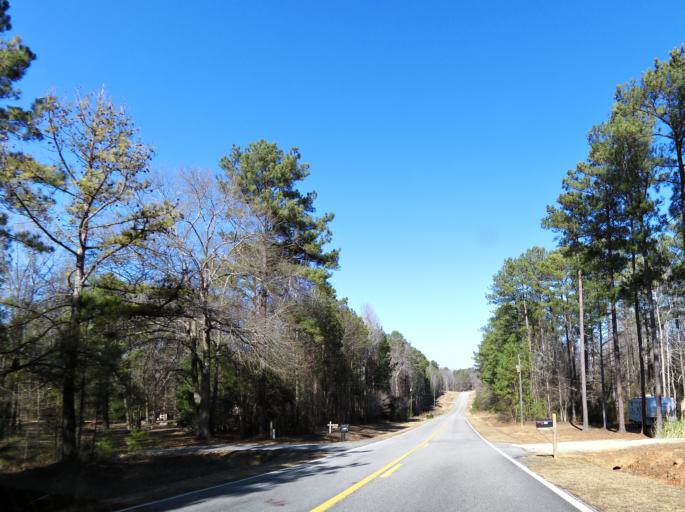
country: US
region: Georgia
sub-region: Bibb County
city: West Point
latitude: 32.8202
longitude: -83.8420
